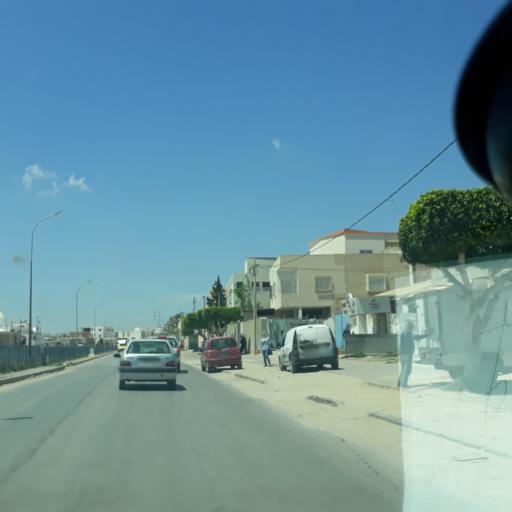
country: TN
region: Safaqis
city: Al Qarmadah
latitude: 34.8071
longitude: 10.7535
